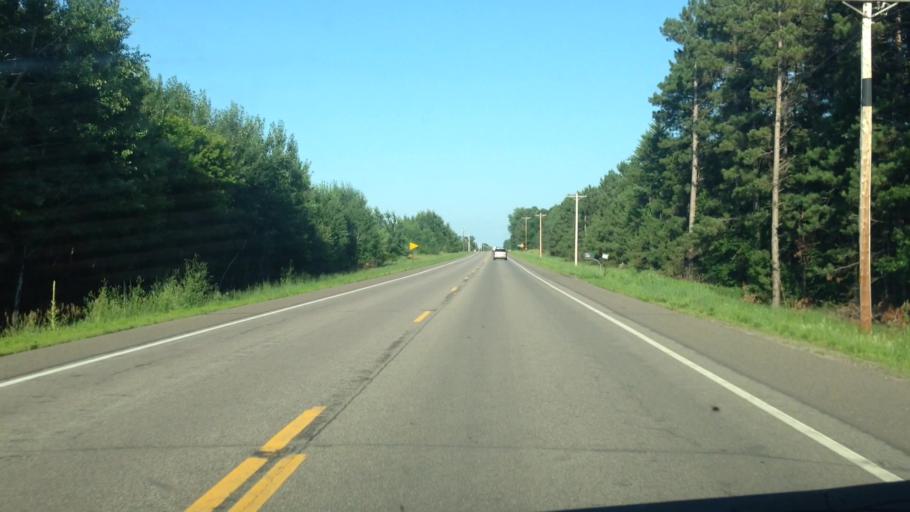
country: US
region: Minnesota
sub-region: Sherburne County
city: Big Lake
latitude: 45.4477
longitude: -93.7319
